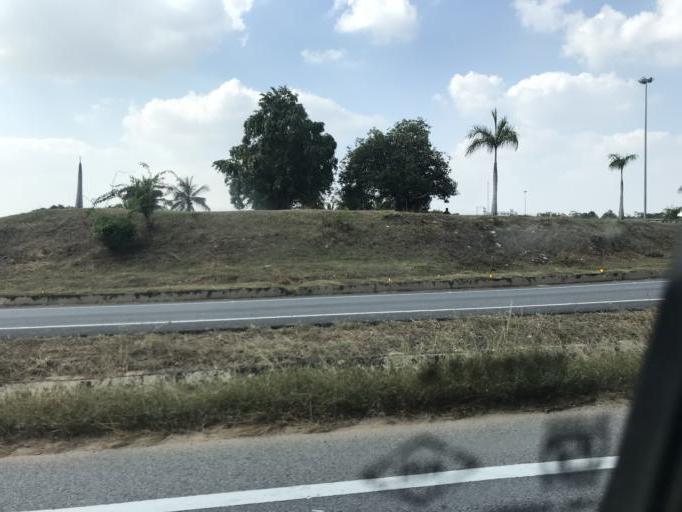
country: IN
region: Karnataka
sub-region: Bangalore Urban
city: Bangalore
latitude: 12.8784
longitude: 77.4964
